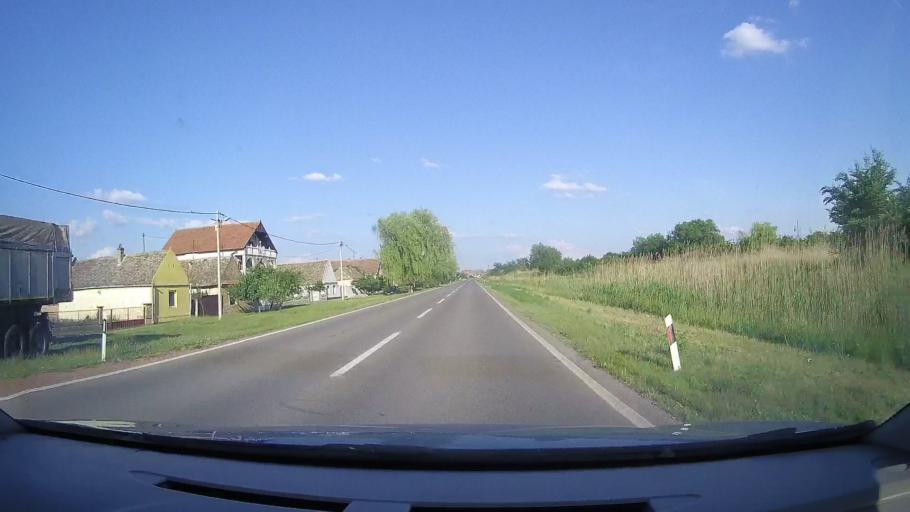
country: RS
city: Nikolinci
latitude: 45.0548
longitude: 21.0519
